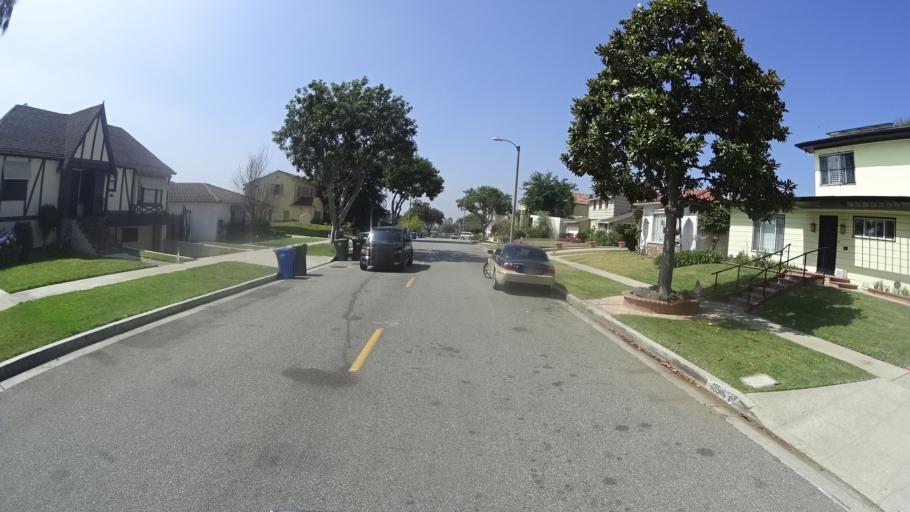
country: US
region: California
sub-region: Los Angeles County
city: View Park-Windsor Hills
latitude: 33.9993
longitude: -118.3432
